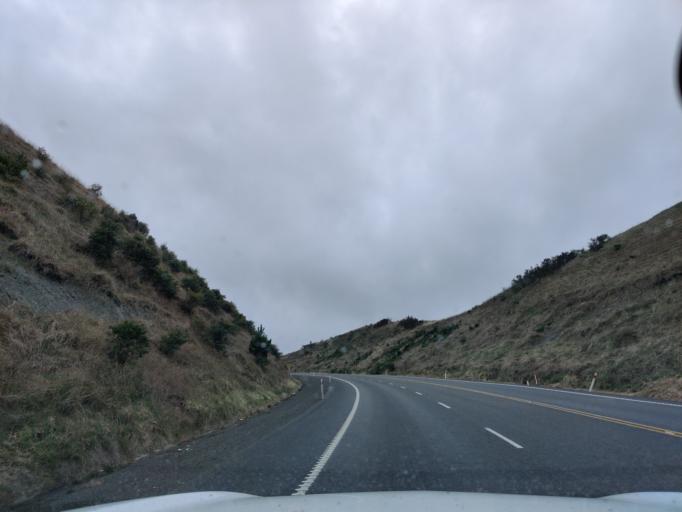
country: NZ
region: Manawatu-Wanganui
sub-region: Ruapehu District
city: Waiouru
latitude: -39.5972
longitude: 175.7648
